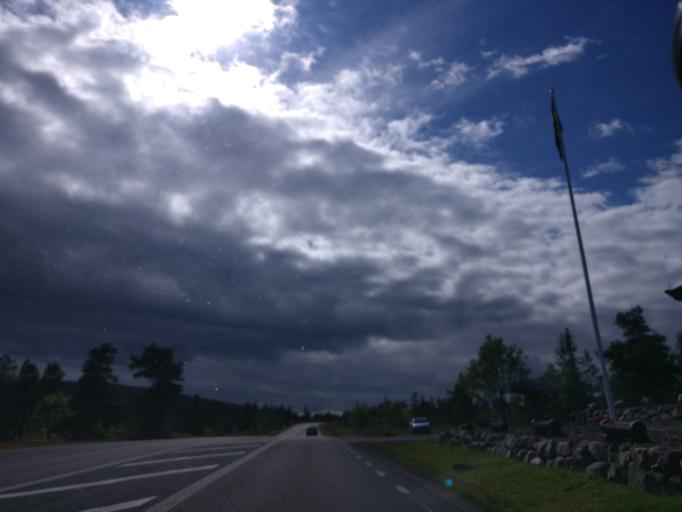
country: SE
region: Dalarna
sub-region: Malung-Saelens kommun
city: Malung
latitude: 61.1584
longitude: 13.1342
